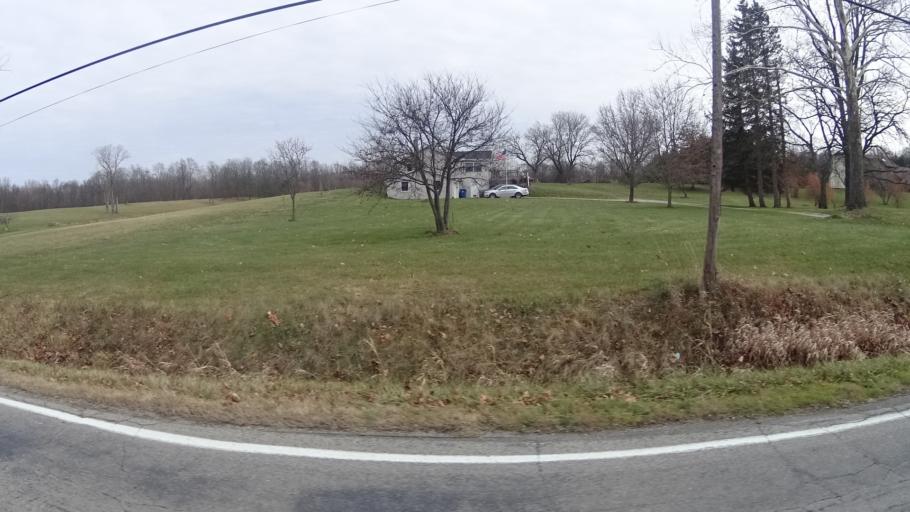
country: US
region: Ohio
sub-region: Lorain County
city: Wellington
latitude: 41.1798
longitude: -82.2687
